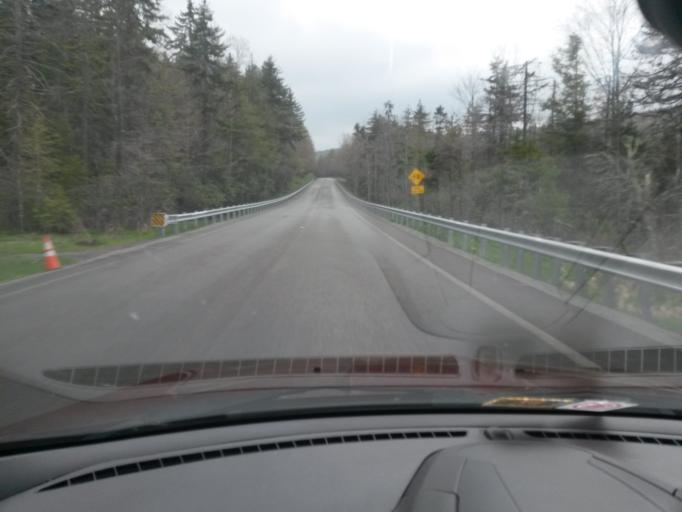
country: US
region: West Virginia
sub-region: Randolph County
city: Elkins
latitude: 38.6250
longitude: -79.8989
